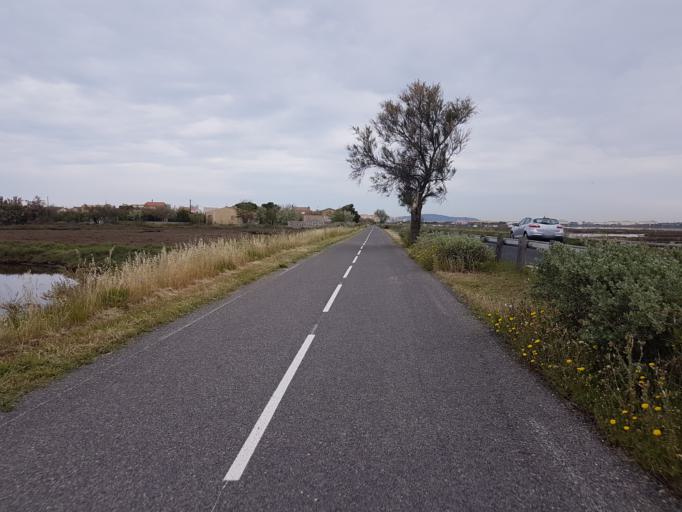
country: FR
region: Languedoc-Roussillon
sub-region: Departement de l'Herault
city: Frontignan
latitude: 43.4385
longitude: 3.7844
